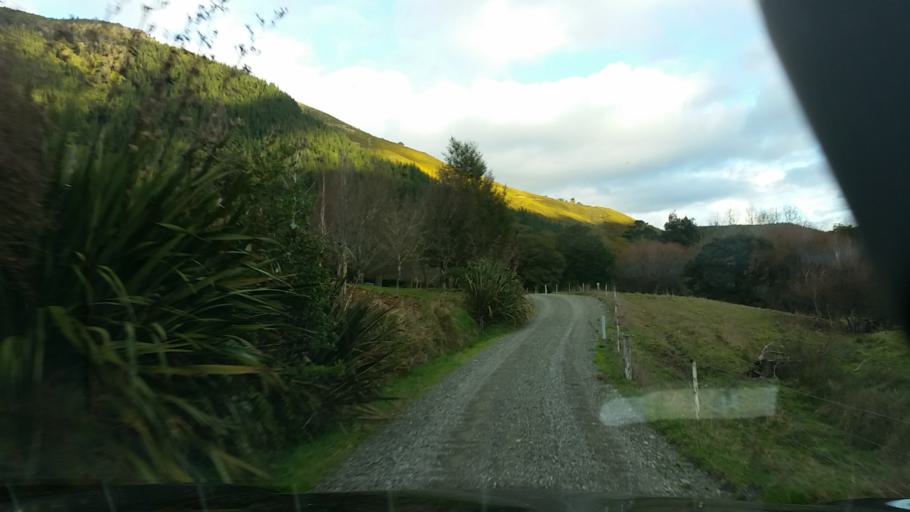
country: NZ
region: Marlborough
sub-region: Marlborough District
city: Picton
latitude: -41.1775
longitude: 173.6497
